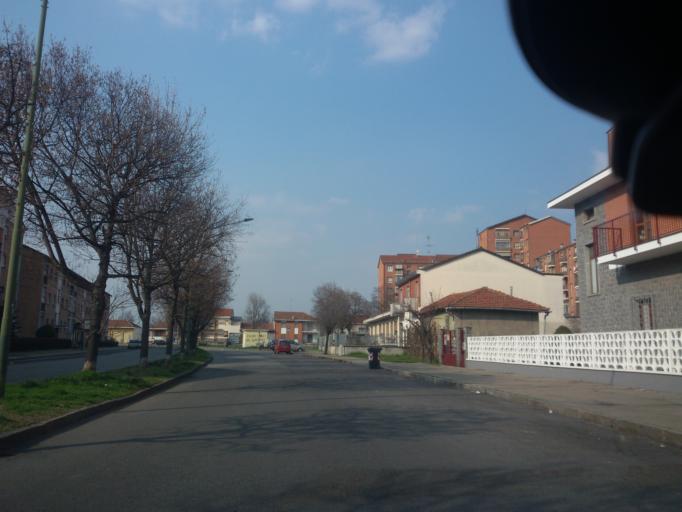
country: IT
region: Piedmont
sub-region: Provincia di Torino
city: Venaria Reale
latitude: 45.1046
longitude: 7.6361
